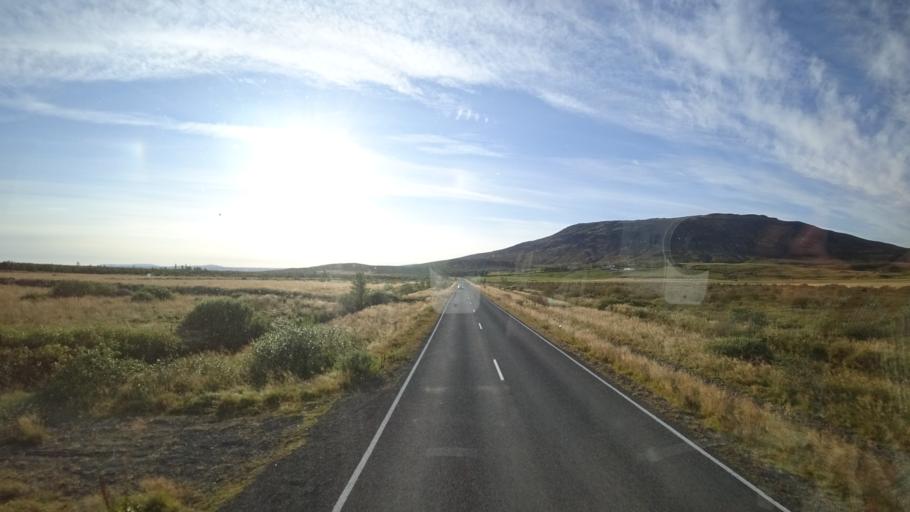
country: IS
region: South
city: Selfoss
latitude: 64.2399
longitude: -20.5290
